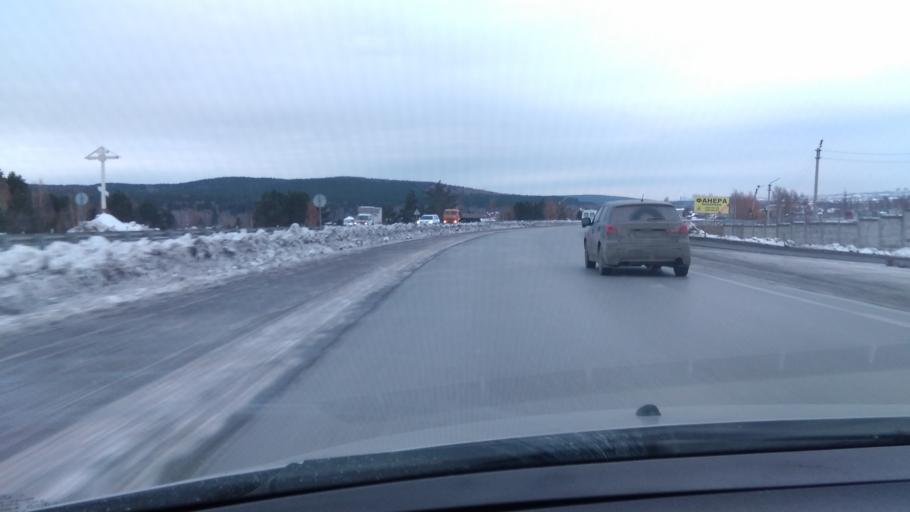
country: RU
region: Sverdlovsk
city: Aramil
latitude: 56.6951
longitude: 60.7530
